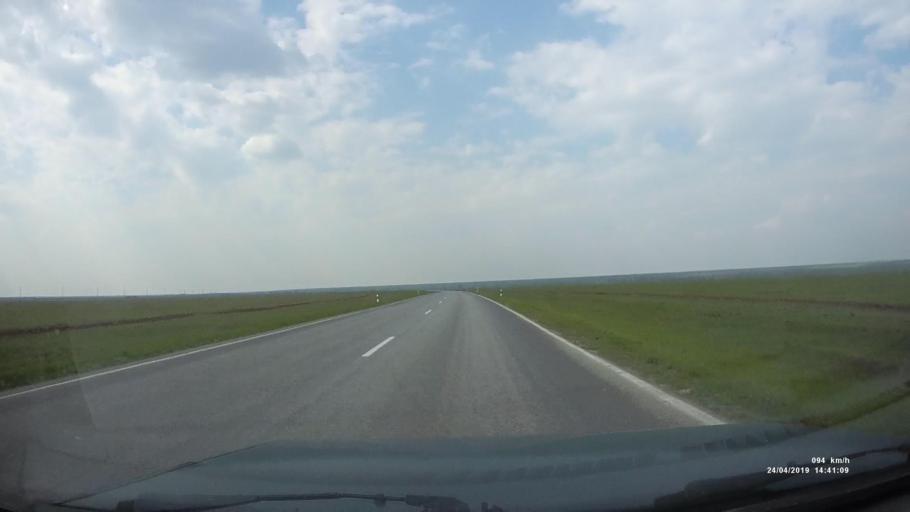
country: RU
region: Rostov
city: Remontnoye
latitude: 46.4418
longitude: 43.8830
